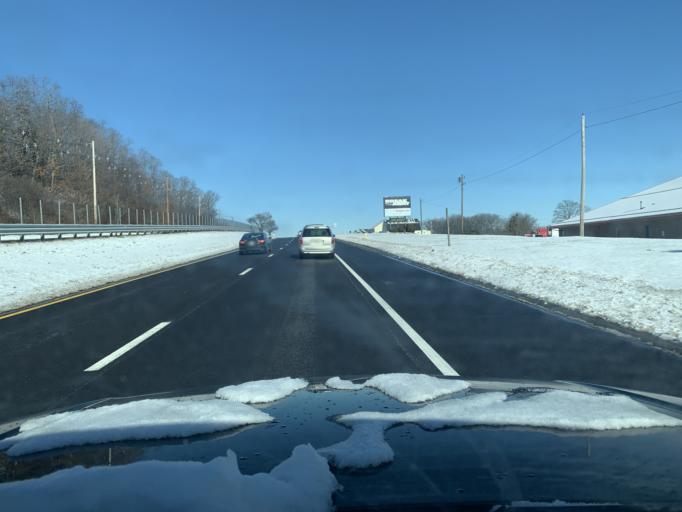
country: US
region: Massachusetts
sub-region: Essex County
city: Danvers
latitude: 42.5775
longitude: -70.9697
